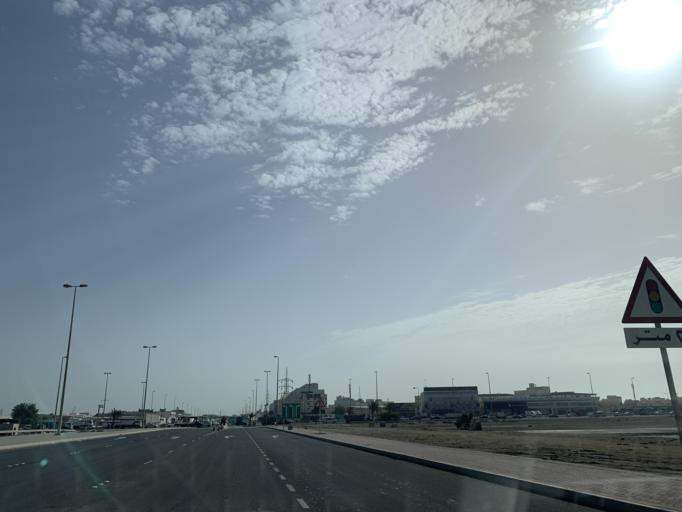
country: BH
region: Northern
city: Sitrah
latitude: 26.1705
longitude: 50.5992
